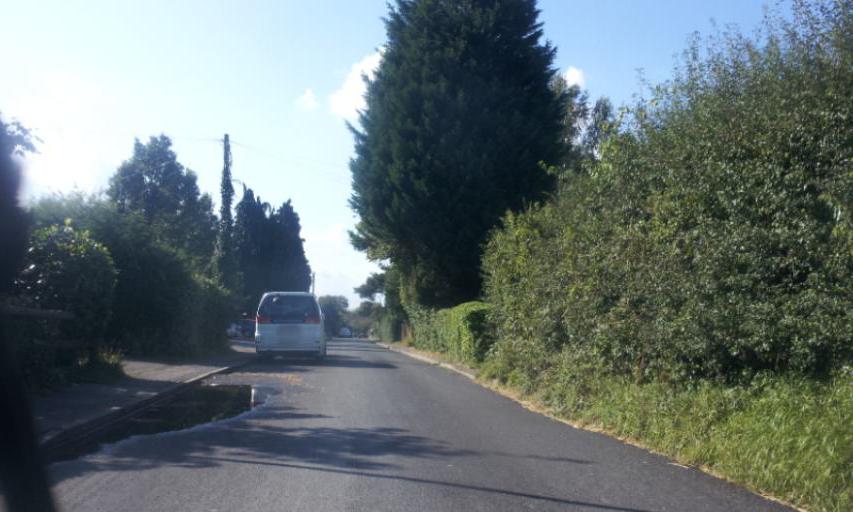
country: GB
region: England
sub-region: Kent
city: Hadlow
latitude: 51.2235
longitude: 0.3429
